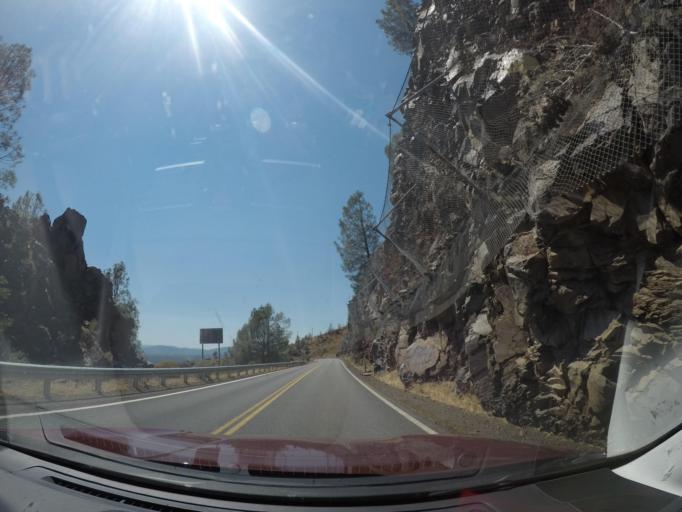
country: US
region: California
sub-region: Shasta County
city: Burney
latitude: 40.9935
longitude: -121.4883
